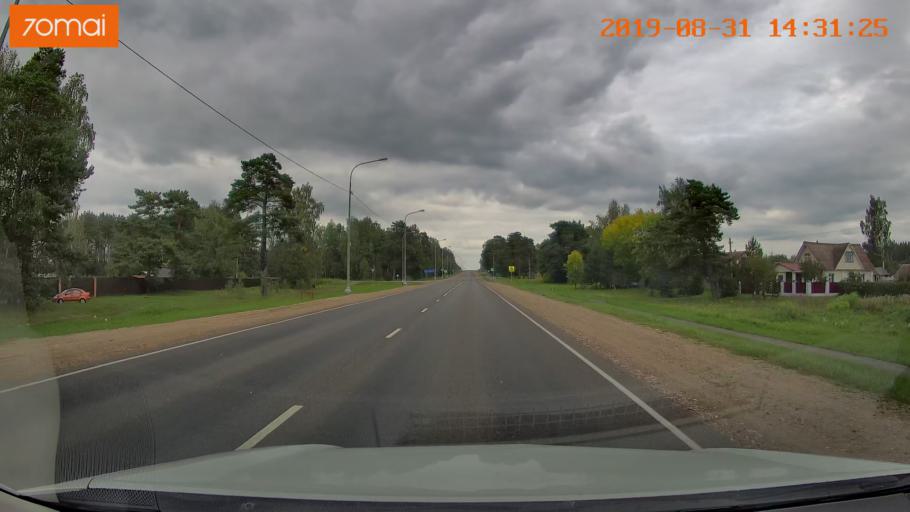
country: RU
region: Smolensk
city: Yekimovichi
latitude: 54.1379
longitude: 33.3722
